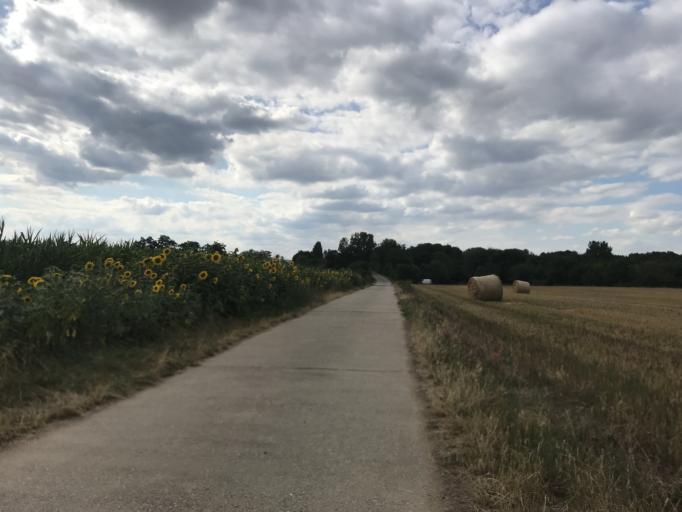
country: DE
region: Hesse
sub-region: Regierungsbezirk Darmstadt
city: Hochheim am Main
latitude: 50.0215
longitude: 8.3383
